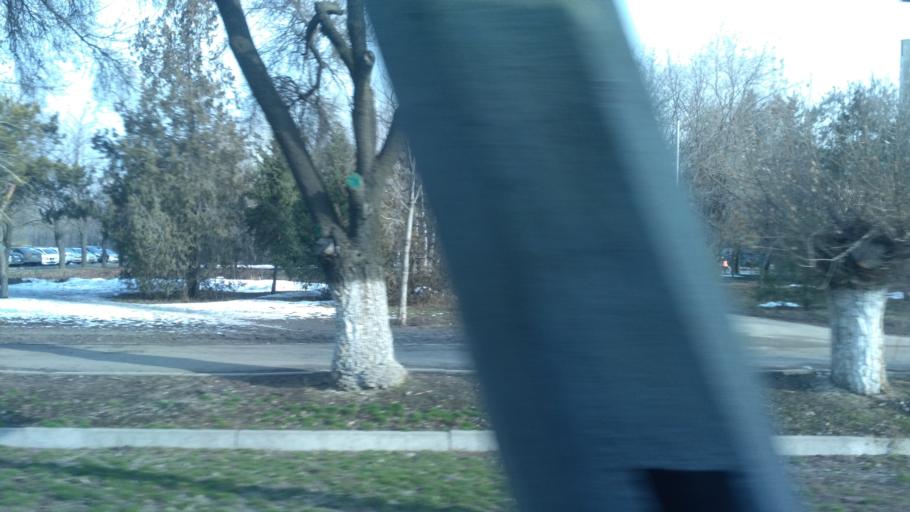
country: KZ
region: Almaty Qalasy
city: Almaty
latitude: 43.2269
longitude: 76.9238
